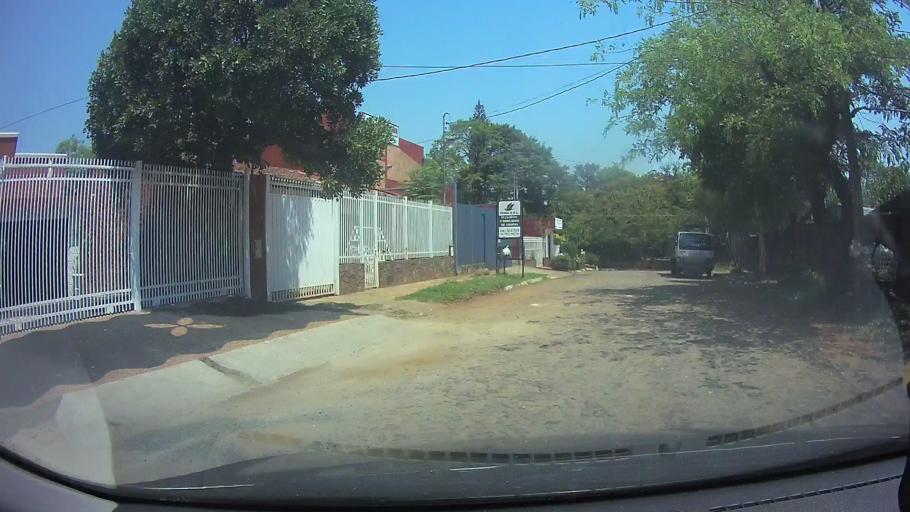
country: PY
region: Central
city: Fernando de la Mora
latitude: -25.3297
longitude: -57.5450
